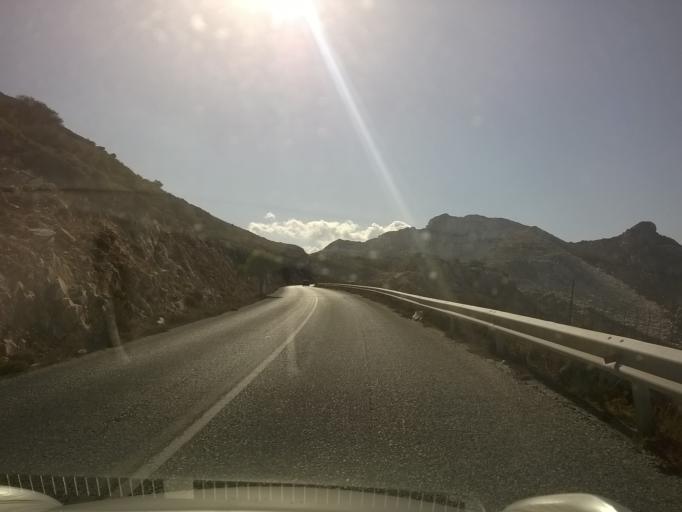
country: GR
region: South Aegean
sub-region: Nomos Kykladon
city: Filotion
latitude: 37.0948
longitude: 25.4661
